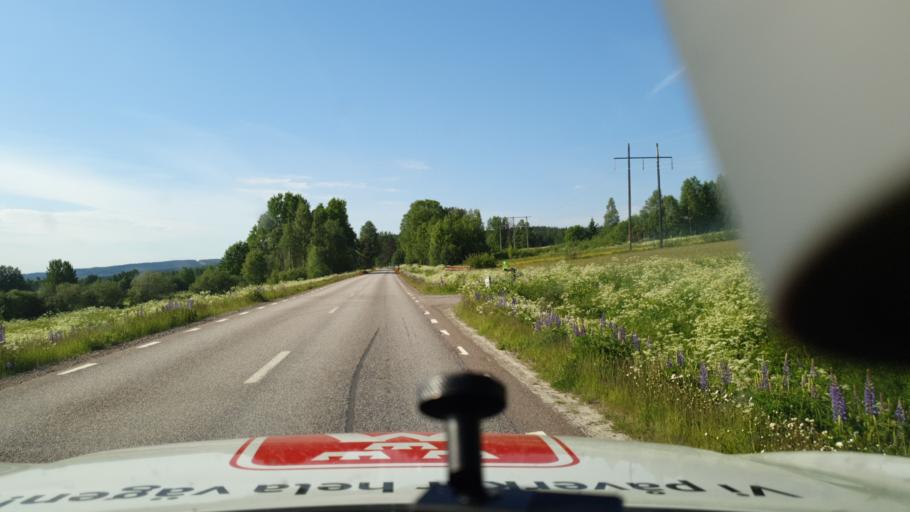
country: SE
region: Vaermland
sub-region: Torsby Kommun
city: Torsby
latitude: 59.9297
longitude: 12.8985
